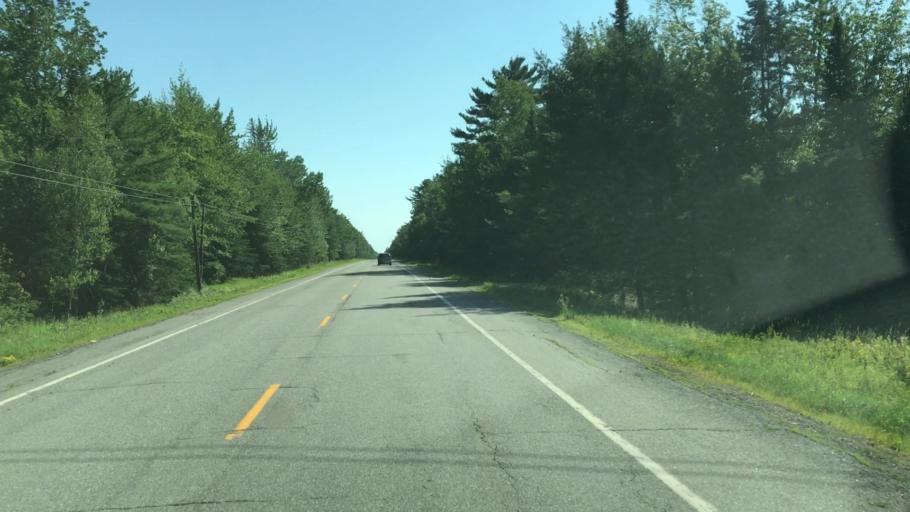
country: US
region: Maine
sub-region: Penobscot County
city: Enfield
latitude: 45.3168
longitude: -68.6024
